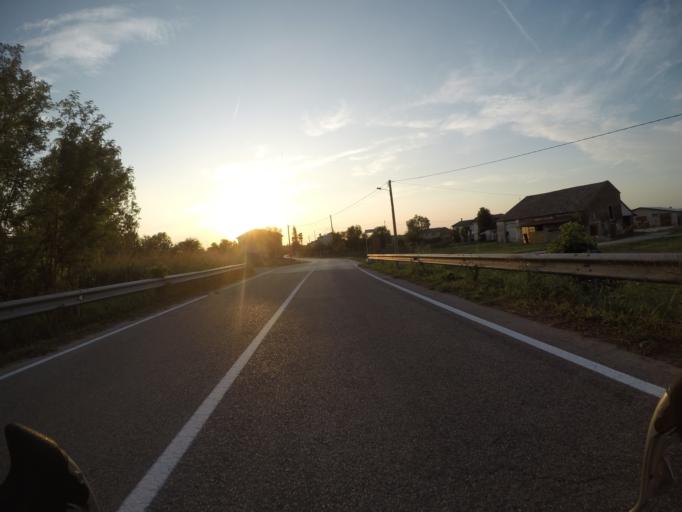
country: IT
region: Veneto
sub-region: Provincia di Rovigo
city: San Bellino
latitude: 45.0027
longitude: 11.5777
